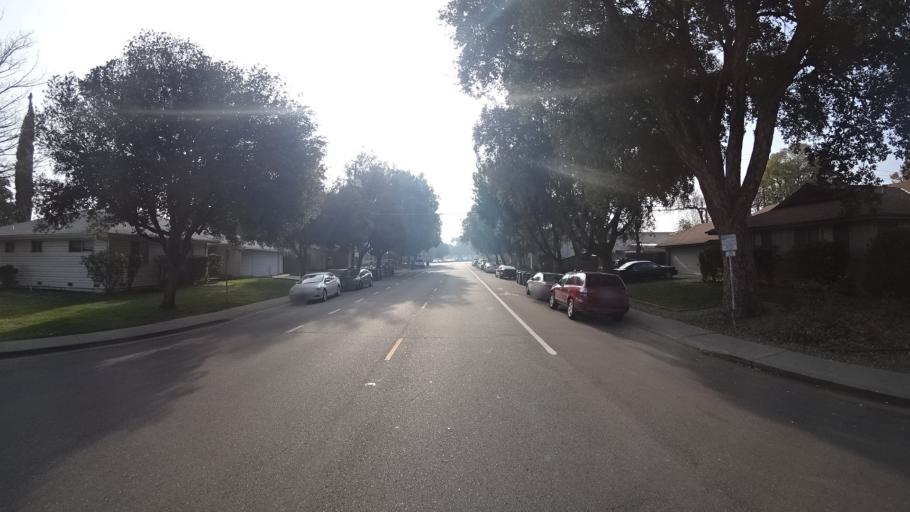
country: US
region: California
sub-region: Yolo County
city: Davis
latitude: 38.5495
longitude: -121.7631
